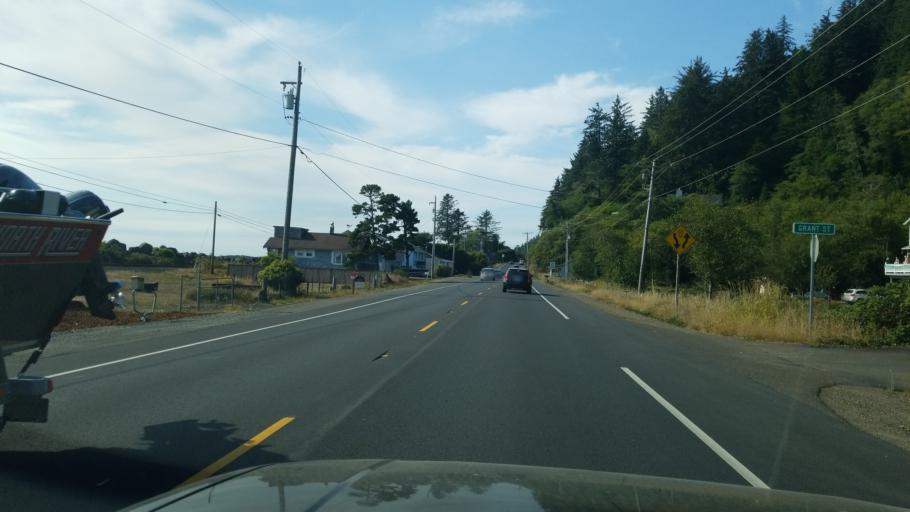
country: US
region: Oregon
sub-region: Tillamook County
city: Rockaway Beach
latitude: 45.5653
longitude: -123.9378
